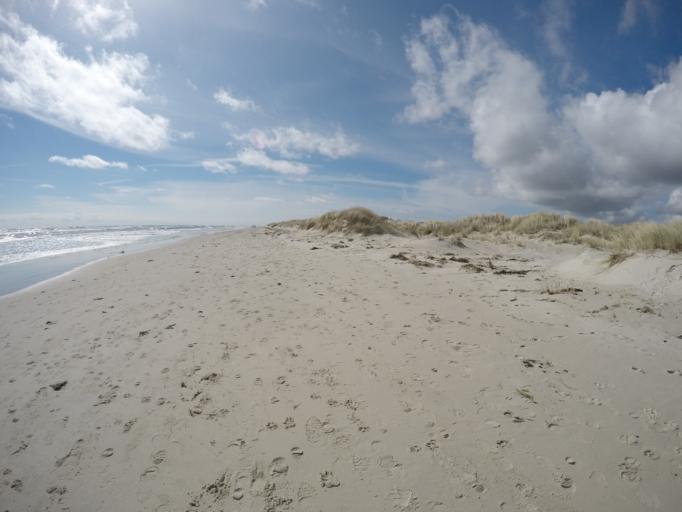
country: SE
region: Skane
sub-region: Simrishamns Kommun
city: Simrishamn
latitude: 55.4052
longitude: 14.2180
